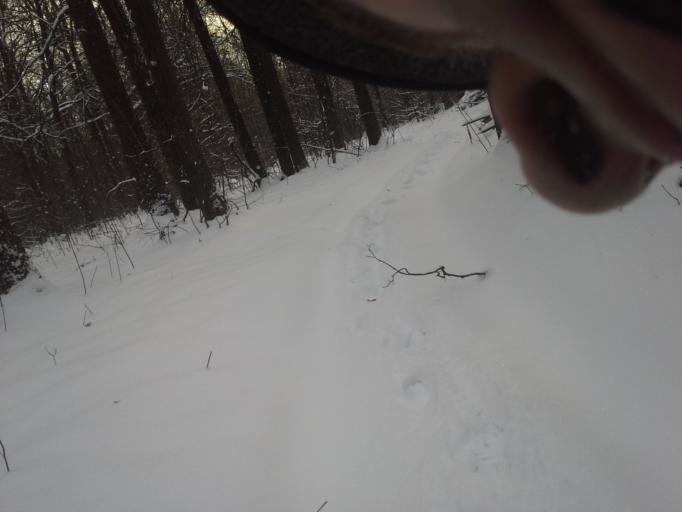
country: RU
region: Moskovskaya
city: Kommunarka
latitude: 55.5825
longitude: 37.4980
